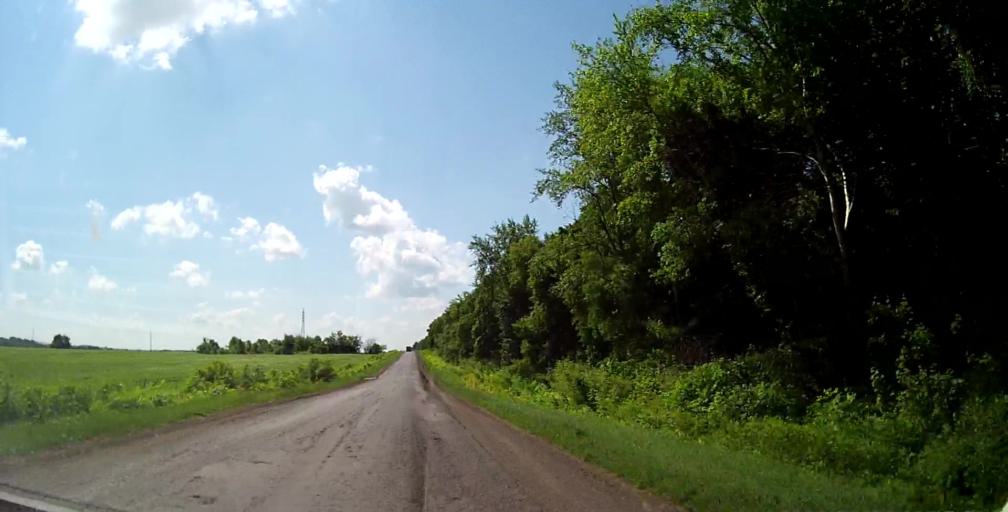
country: RU
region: Lipetsk
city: Chaplygin
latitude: 53.2955
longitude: 39.9557
